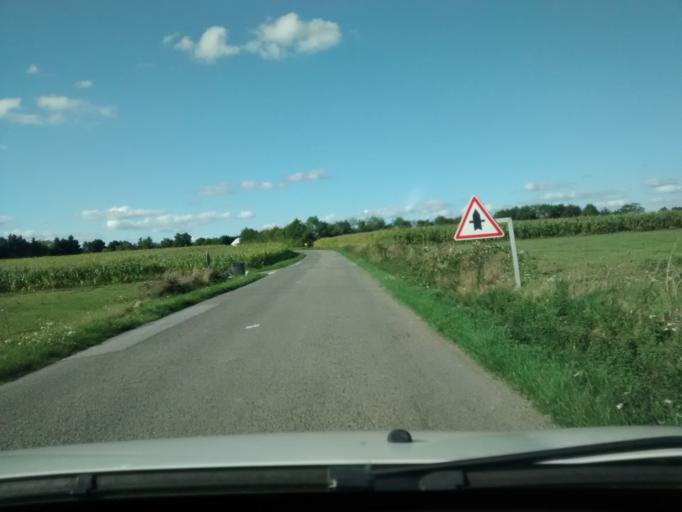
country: FR
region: Brittany
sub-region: Departement d'Ille-et-Vilaine
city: Noyal-sur-Vilaine
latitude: 48.0820
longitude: -1.5464
